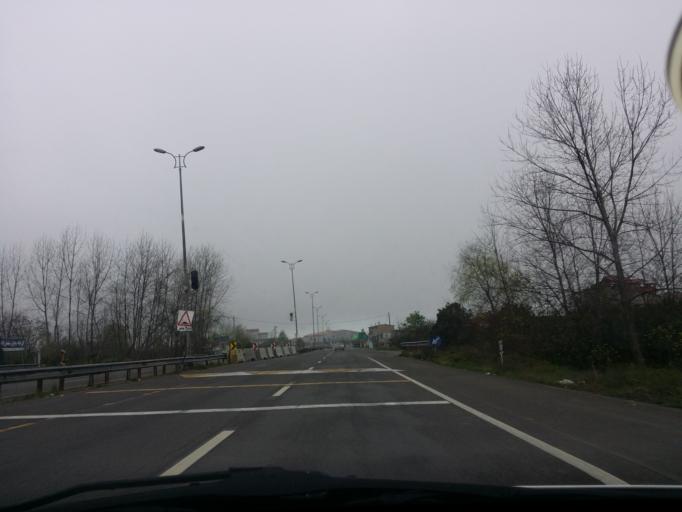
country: IR
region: Mazandaran
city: Tonekabon
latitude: 36.8361
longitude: 50.8367
